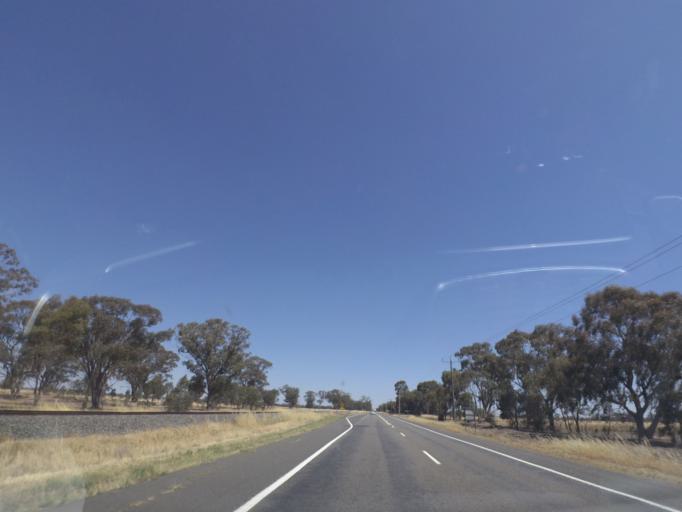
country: AU
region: Victoria
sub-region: Greater Shepparton
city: Shepparton
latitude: -36.1979
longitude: 145.4318
